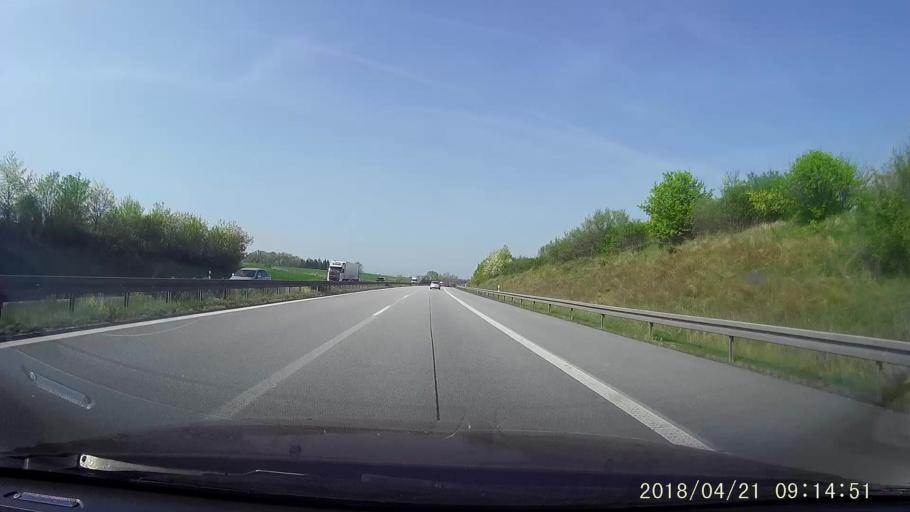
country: DE
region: Saxony
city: Reichenbach
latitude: 51.2062
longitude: 14.7842
